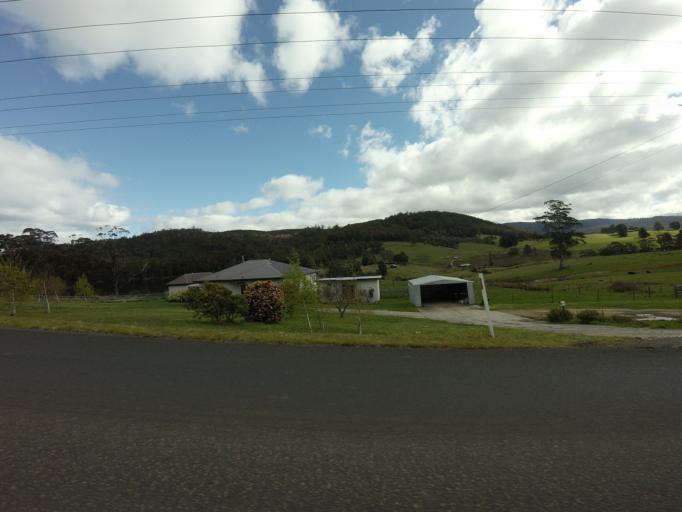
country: AU
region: Tasmania
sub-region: Huon Valley
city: Geeveston
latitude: -43.1850
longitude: 146.9313
